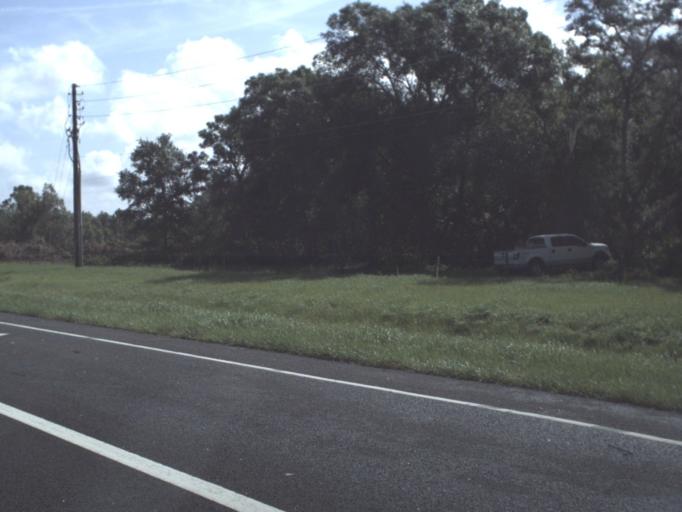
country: US
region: Florida
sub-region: Hillsborough County
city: Sun City Center
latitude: 27.6975
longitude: -82.3402
